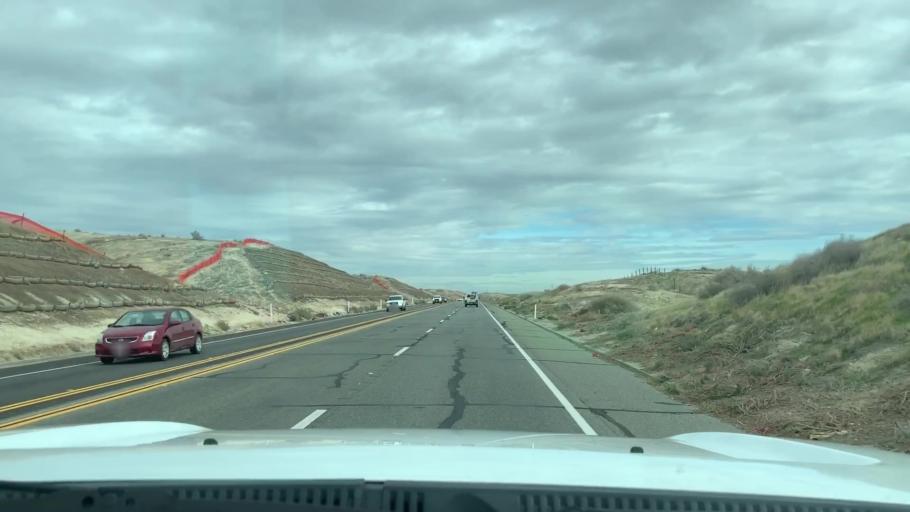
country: US
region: California
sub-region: Kern County
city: Ford City
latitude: 35.2485
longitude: -119.3428
